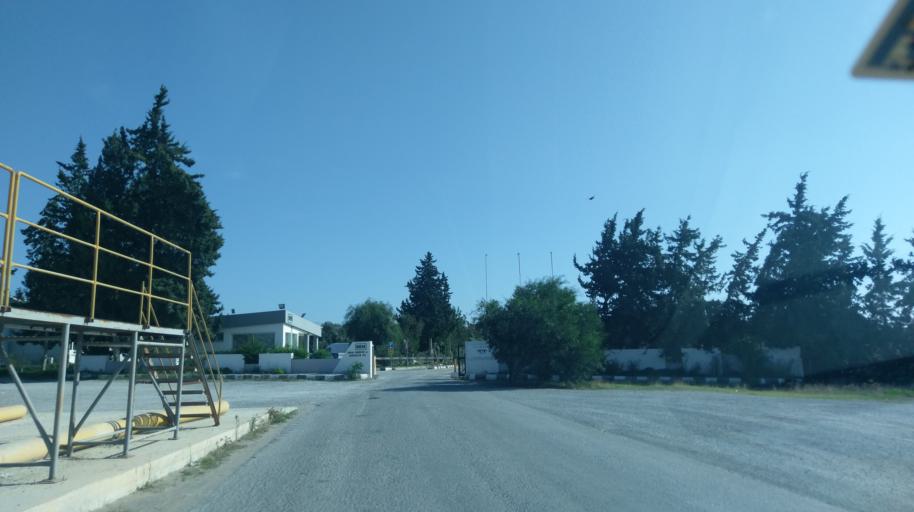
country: CY
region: Ammochostos
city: Trikomo
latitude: 35.3264
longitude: 34.0059
